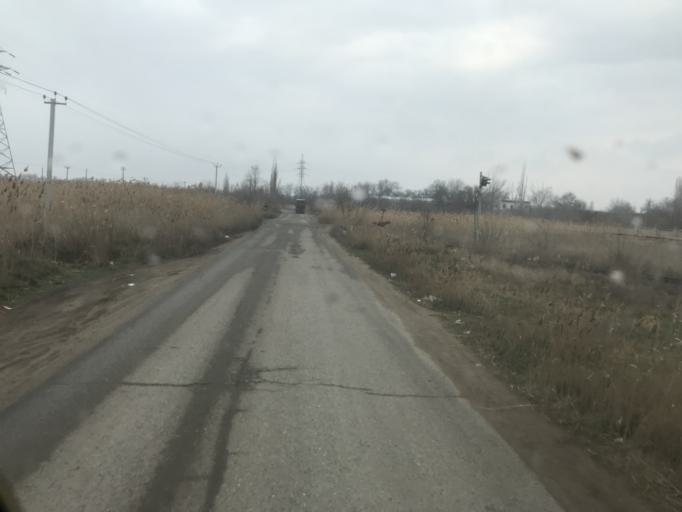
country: RU
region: Volgograd
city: Krasnoslobodsk
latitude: 48.5309
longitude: 44.5952
